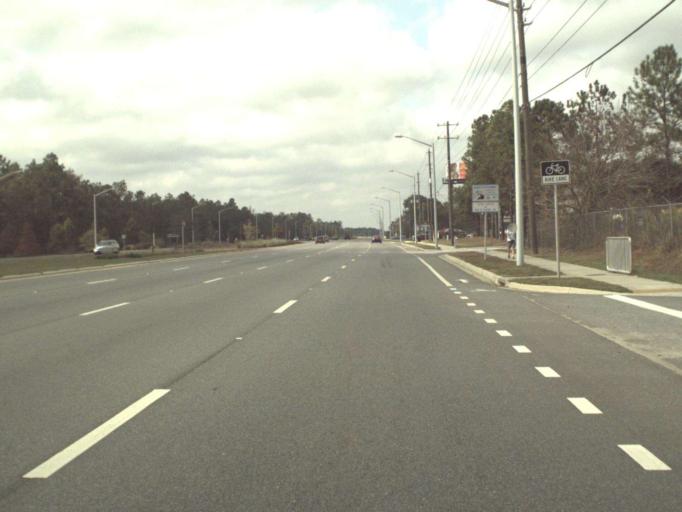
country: US
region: Florida
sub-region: Leon County
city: Tallahassee
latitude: 30.3760
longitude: -84.2727
